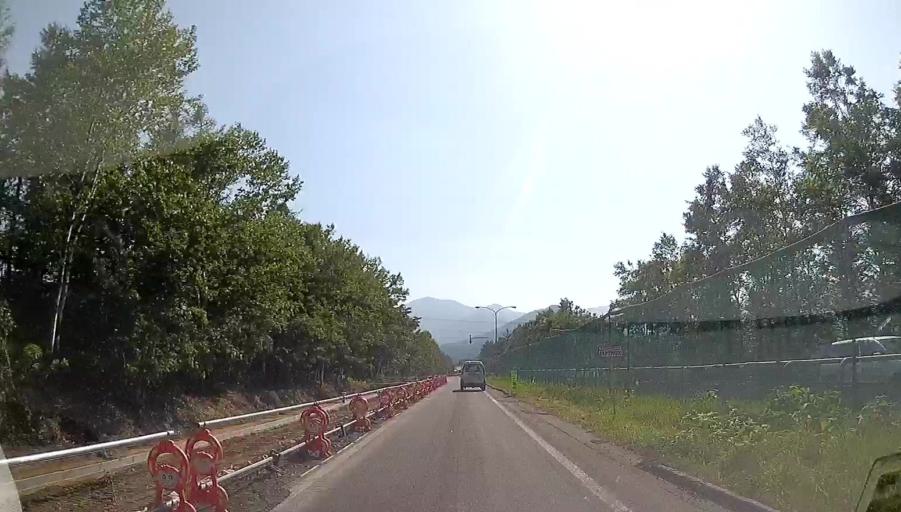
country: JP
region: Hokkaido
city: Otofuke
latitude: 42.9798
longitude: 142.8306
